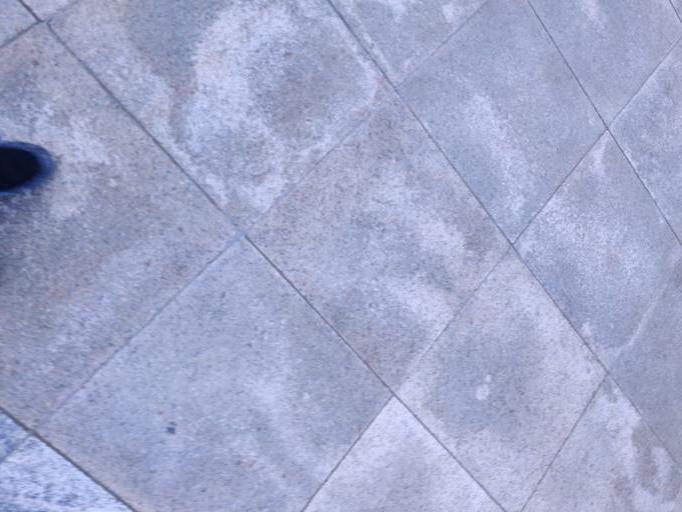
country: SA
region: Al Madinah al Munawwarah
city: Medina
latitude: 24.4660
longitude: 39.6067
